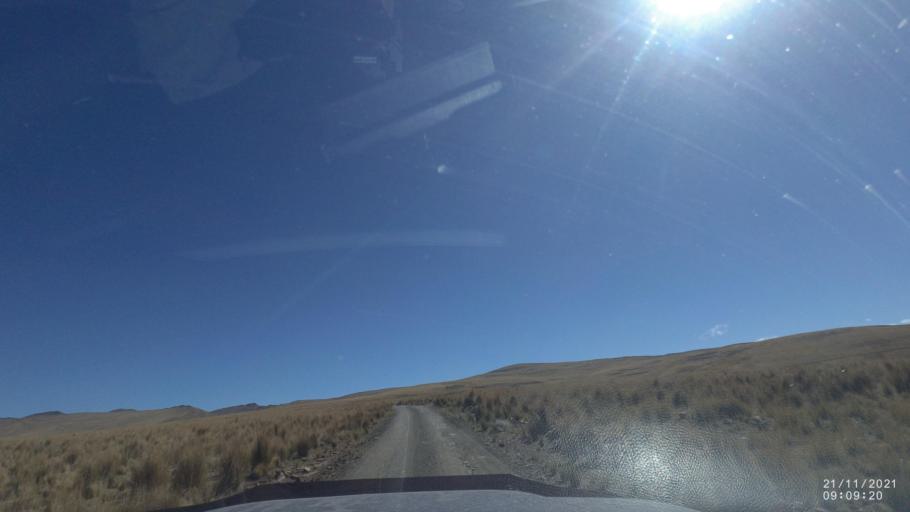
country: BO
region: Cochabamba
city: Cochabamba
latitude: -17.1591
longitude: -66.2619
